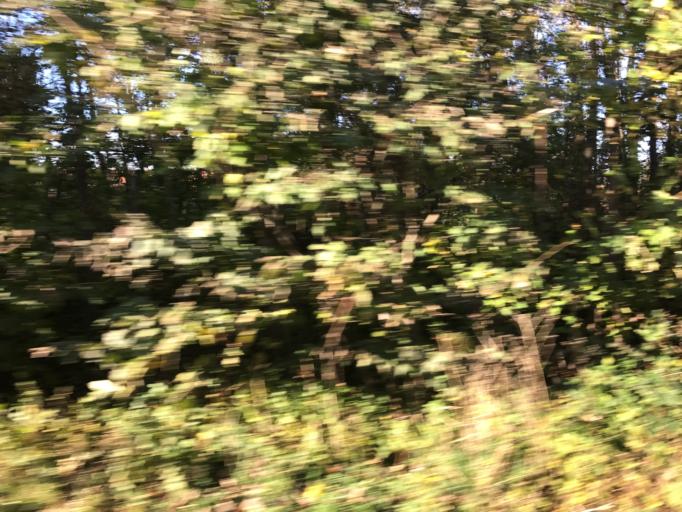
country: DK
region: Zealand
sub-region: Stevns Kommune
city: Store Heddinge
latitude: 55.3110
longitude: 12.3859
